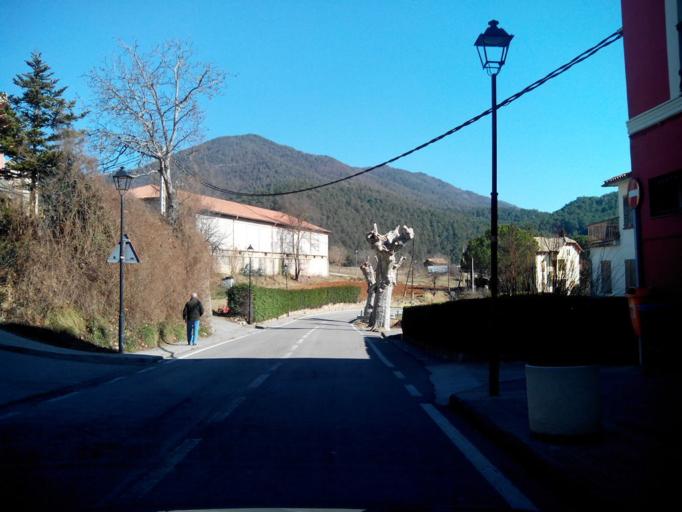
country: ES
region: Catalonia
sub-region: Provincia de Barcelona
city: Vilada
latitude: 42.1374
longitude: 1.9336
